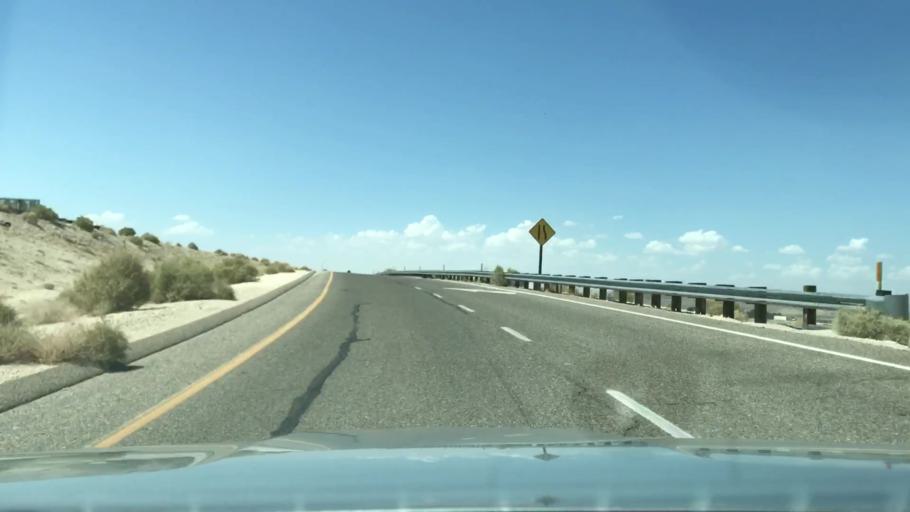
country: US
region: California
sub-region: San Bernardino County
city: Lenwood
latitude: 34.8841
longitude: -117.0895
